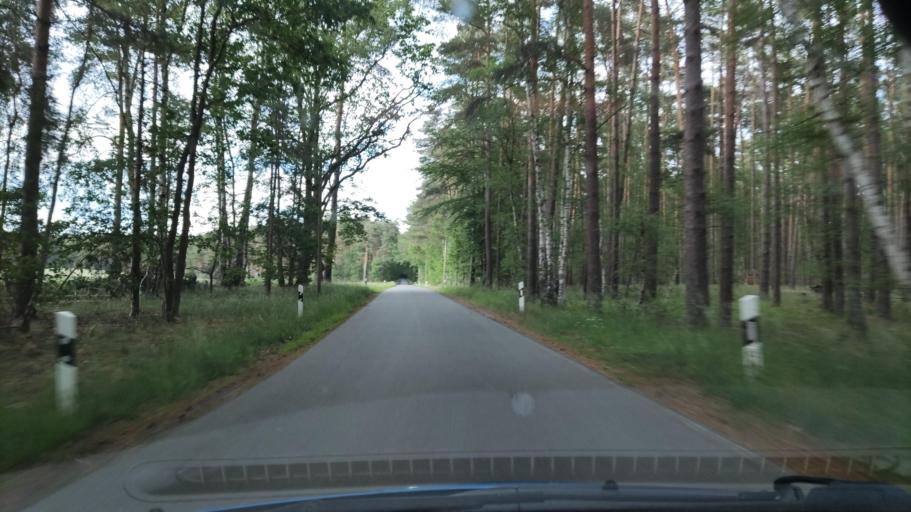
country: DE
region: Lower Saxony
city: Schnega
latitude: 52.9181
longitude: 10.8508
